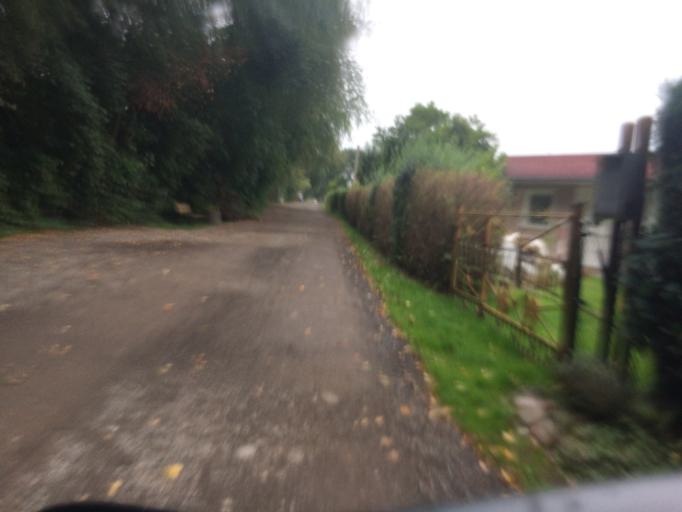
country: DE
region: Berlin
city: Niederschonhausen
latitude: 52.6021
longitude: 13.4096
